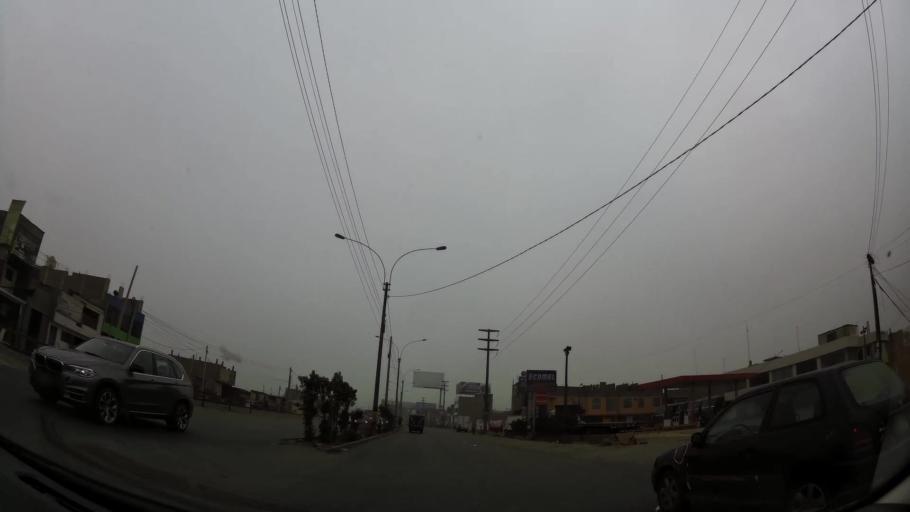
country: PE
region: Lima
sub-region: Lima
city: Santa Maria
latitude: -12.0060
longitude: -76.8480
